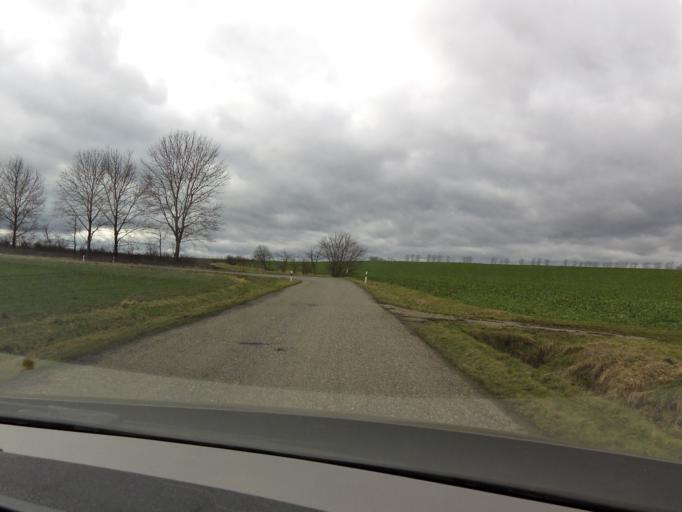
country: DE
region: Thuringia
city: Hammerstedt
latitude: 50.9542
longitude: 11.4486
